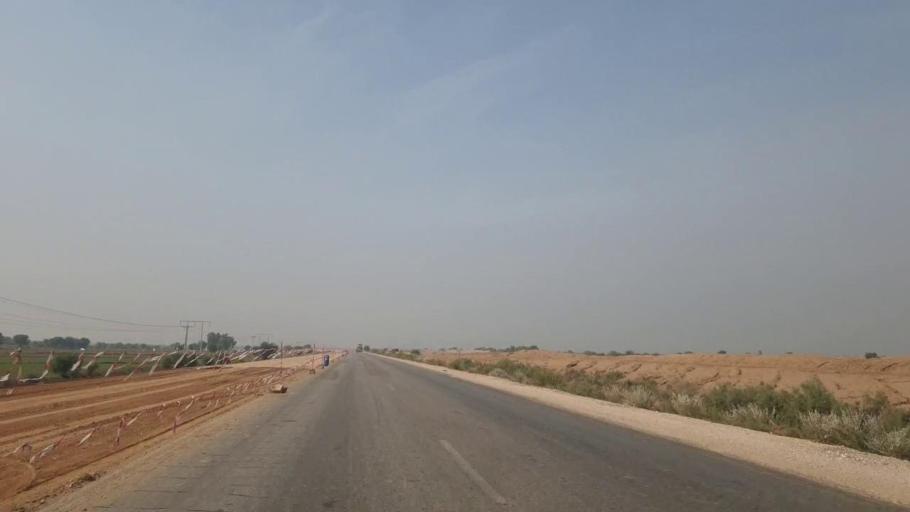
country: PK
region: Sindh
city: Sann
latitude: 26.1370
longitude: 68.0426
